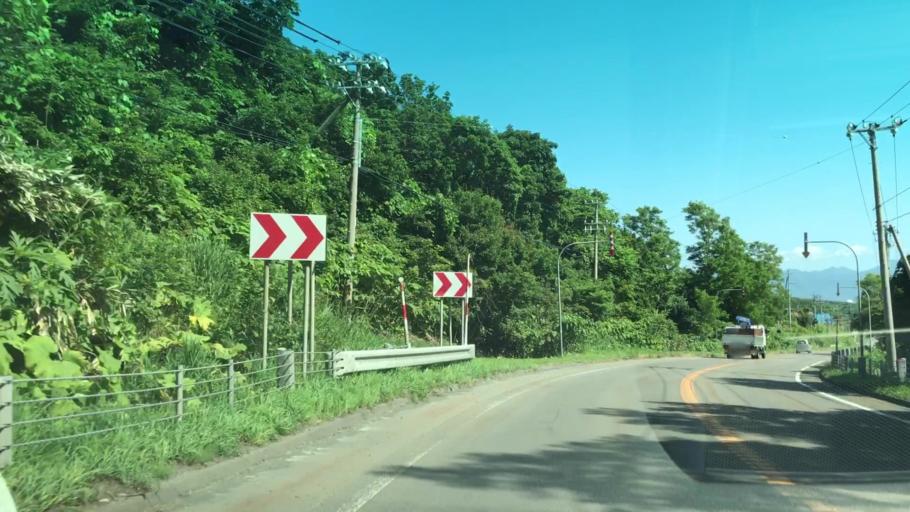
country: JP
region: Hokkaido
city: Iwanai
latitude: 43.0767
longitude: 140.4868
